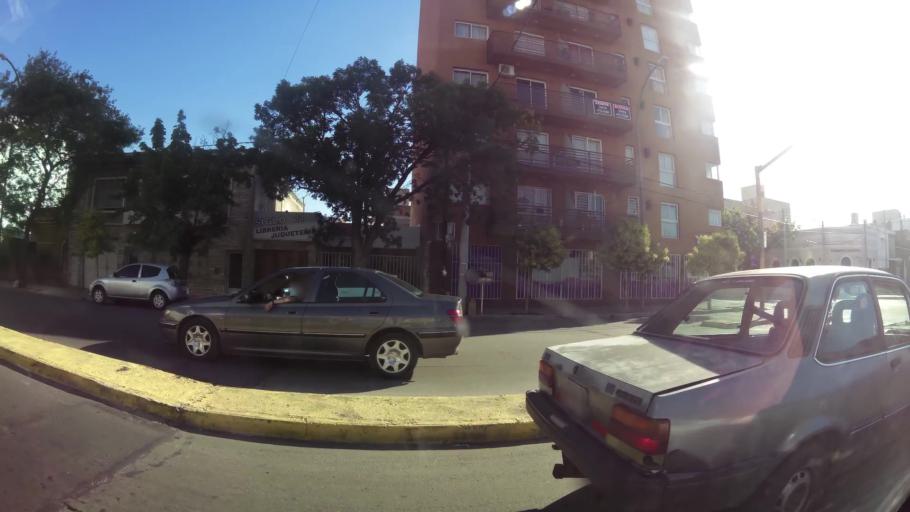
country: AR
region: Cordoba
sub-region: Departamento de Capital
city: Cordoba
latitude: -31.3916
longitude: -64.1824
